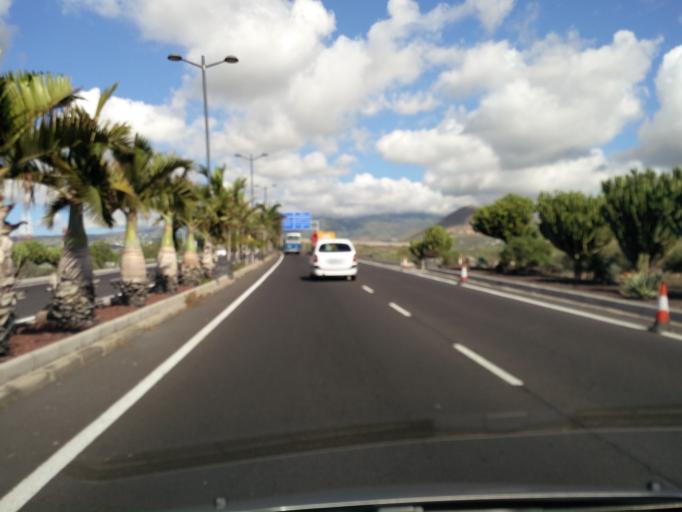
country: ES
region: Canary Islands
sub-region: Provincia de Santa Cruz de Tenerife
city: San Isidro
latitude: 28.0555
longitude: -16.5792
